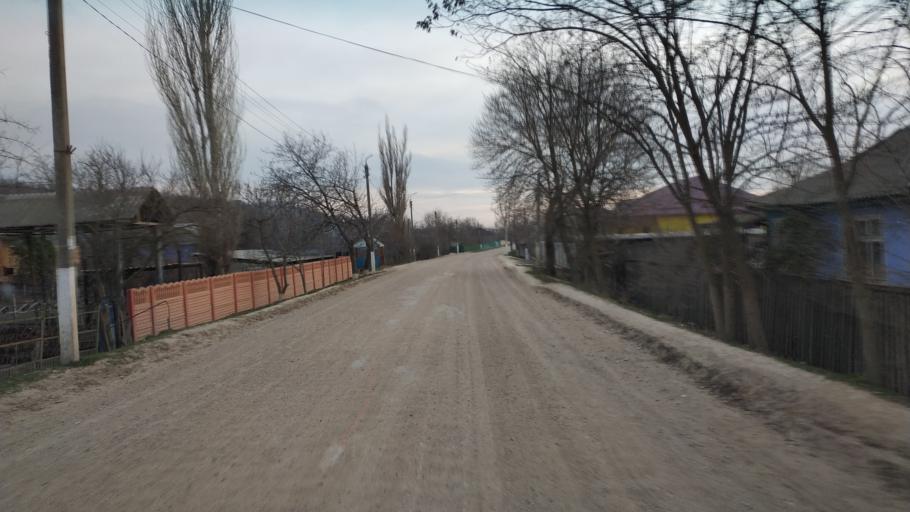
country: MD
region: Hincesti
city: Dancu
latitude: 46.7553
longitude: 28.2079
